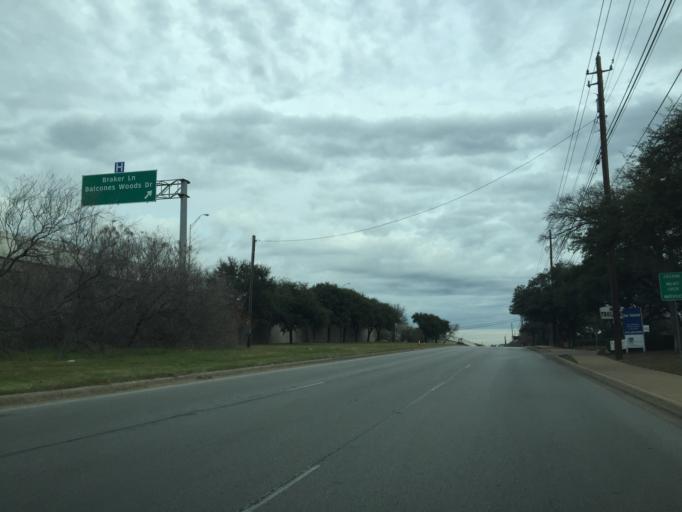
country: US
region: Texas
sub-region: Williamson County
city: Jollyville
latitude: 30.3944
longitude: -97.7459
